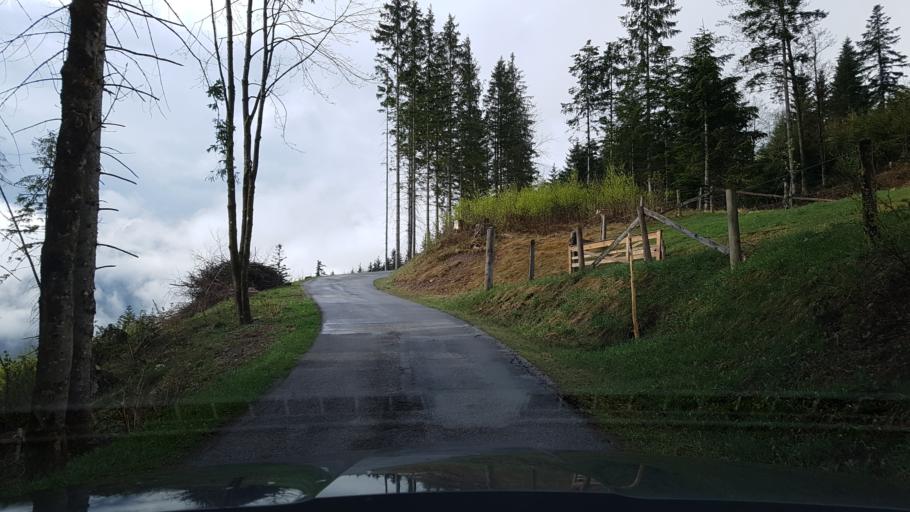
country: AT
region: Salzburg
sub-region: Politischer Bezirk Sankt Johann im Pongau
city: Werfen
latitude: 47.4638
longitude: 13.1777
